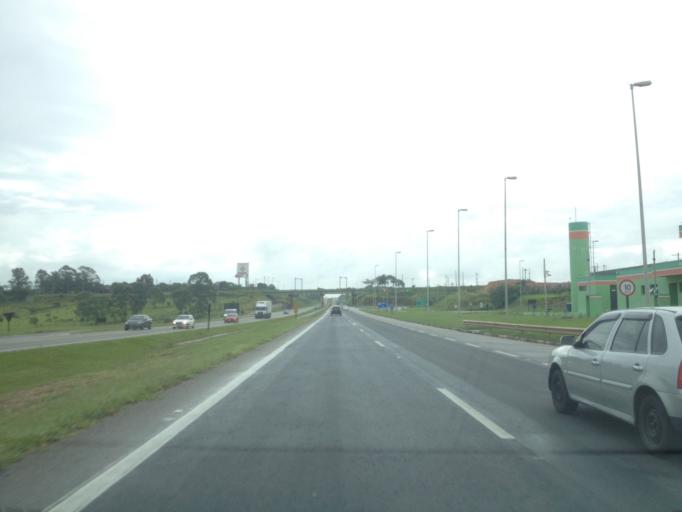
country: BR
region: Sao Paulo
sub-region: Itu
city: Itu
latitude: -23.3656
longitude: -47.3263
